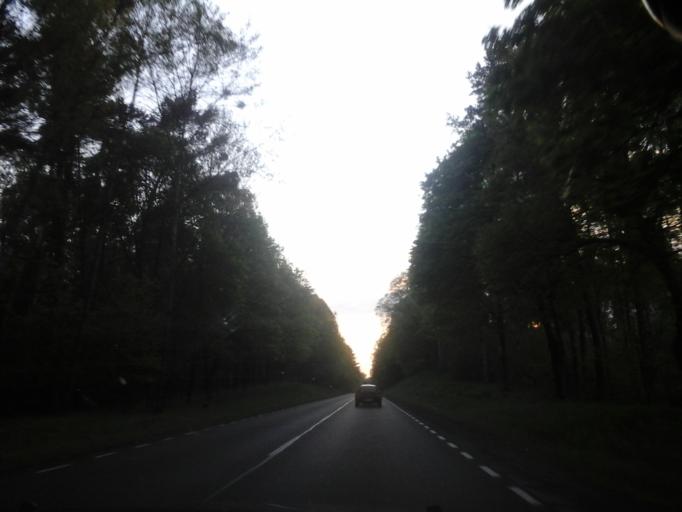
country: PL
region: West Pomeranian Voivodeship
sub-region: Powiat choszczenski
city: Recz
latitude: 53.2818
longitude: 15.6466
